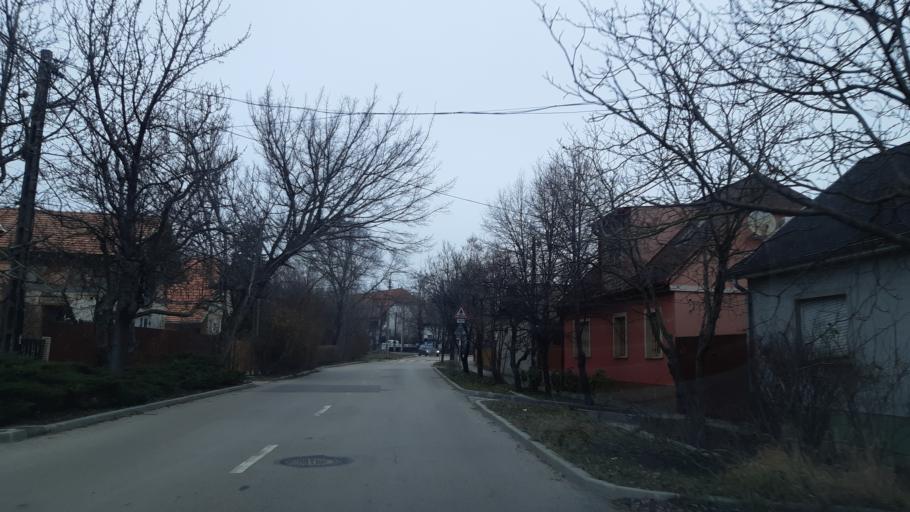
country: HU
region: Pest
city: Budaors
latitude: 47.4567
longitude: 18.9636
